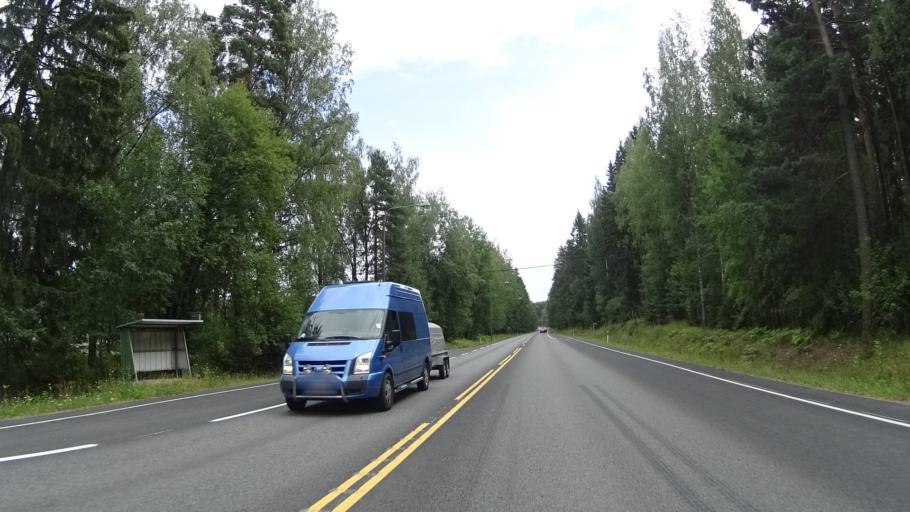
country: FI
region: Pirkanmaa
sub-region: Tampere
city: Kangasala
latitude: 61.4263
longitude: 24.1347
